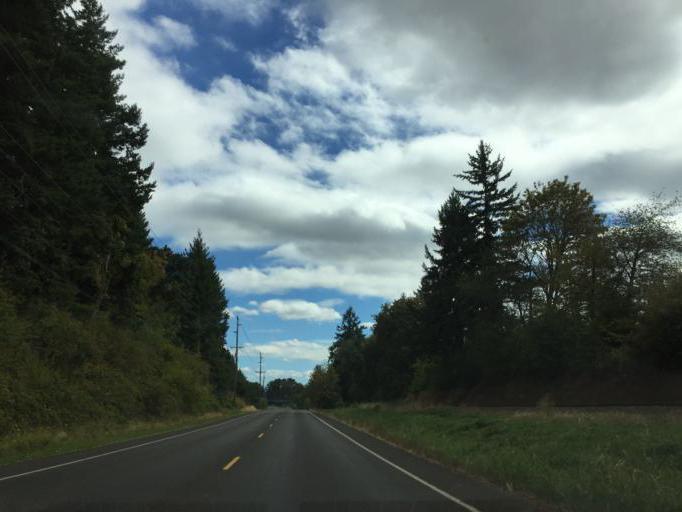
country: US
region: Oregon
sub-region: Marion County
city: Woodburn
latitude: 45.1287
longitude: -122.8269
